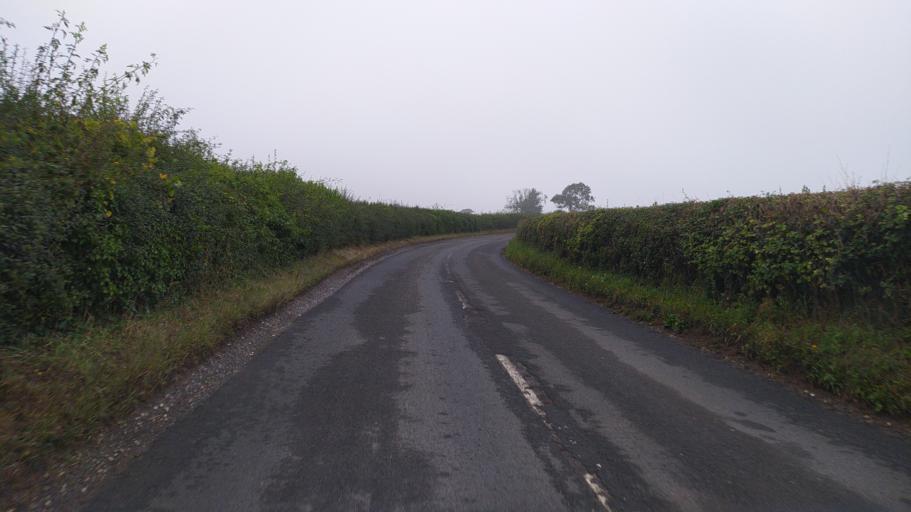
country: GB
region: England
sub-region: Wiltshire
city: Ansty
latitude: 50.9603
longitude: -2.1026
